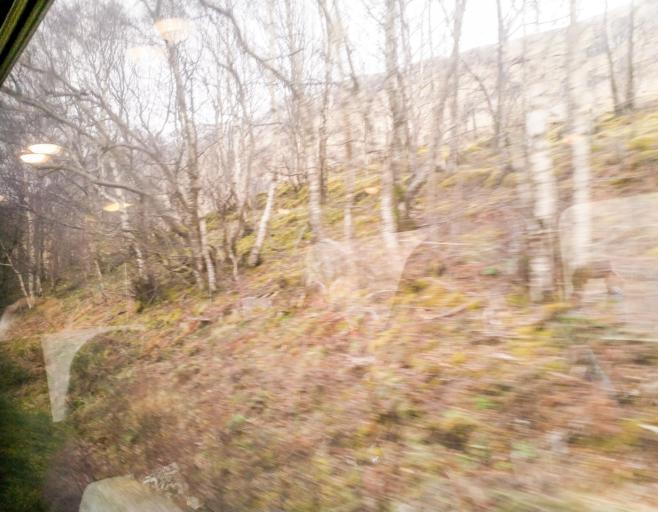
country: GB
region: Scotland
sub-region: Highland
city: Spean Bridge
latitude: 56.8189
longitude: -4.7139
